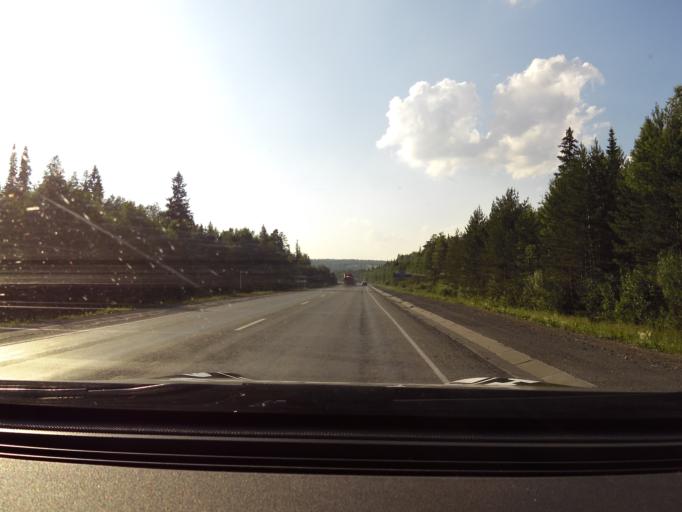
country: RU
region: Sverdlovsk
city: Revda
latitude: 56.8399
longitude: 59.8277
